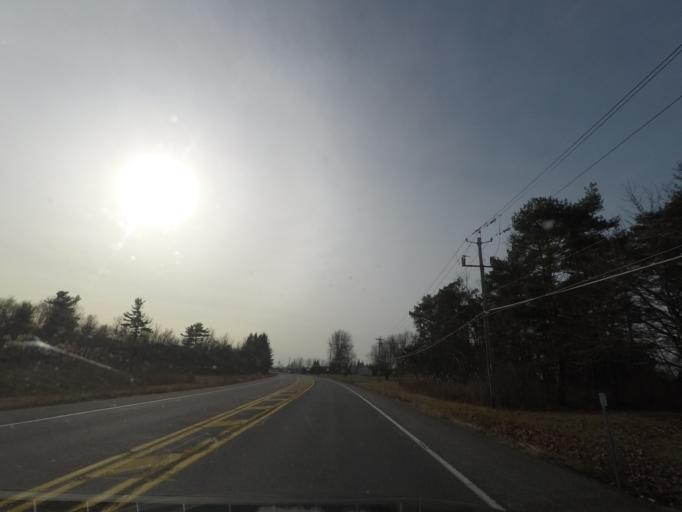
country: US
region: New York
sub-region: Saratoga County
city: Mechanicville
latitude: 42.8826
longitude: -73.7207
